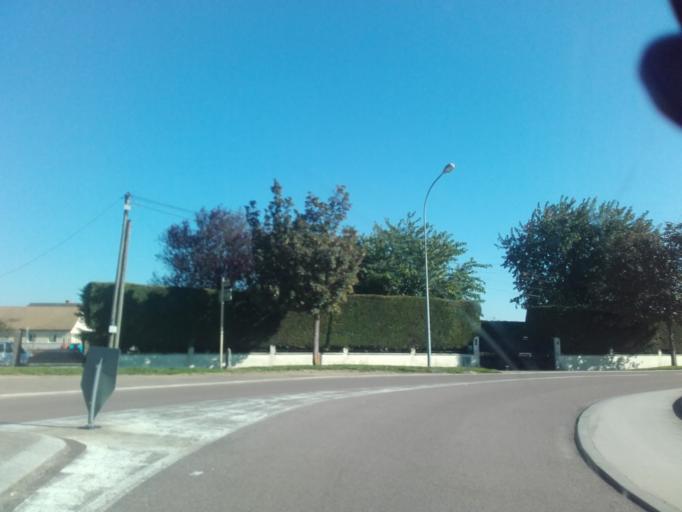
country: FR
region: Bourgogne
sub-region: Departement de la Cote-d'Or
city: Corpeau
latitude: 46.9360
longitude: 4.7546
